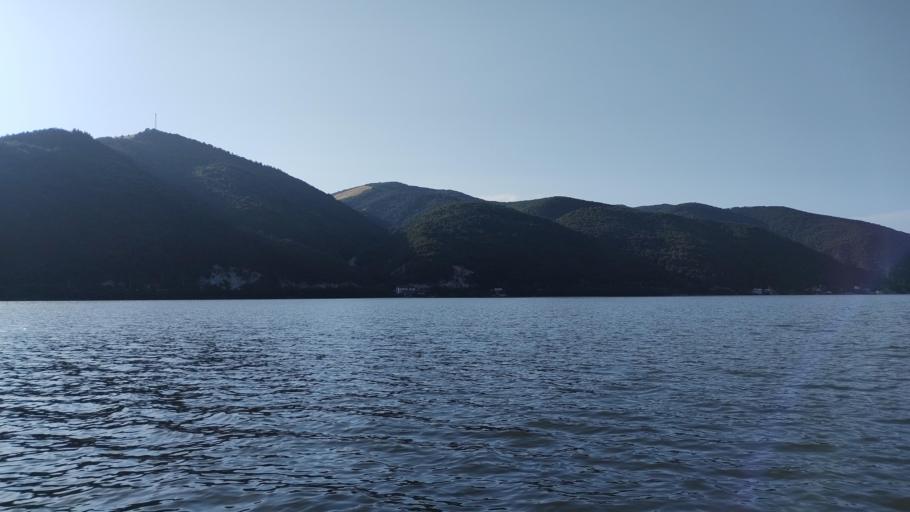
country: RO
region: Mehedinti
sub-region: Comuna Dubova
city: Dubova
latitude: 44.5527
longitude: 22.2284
